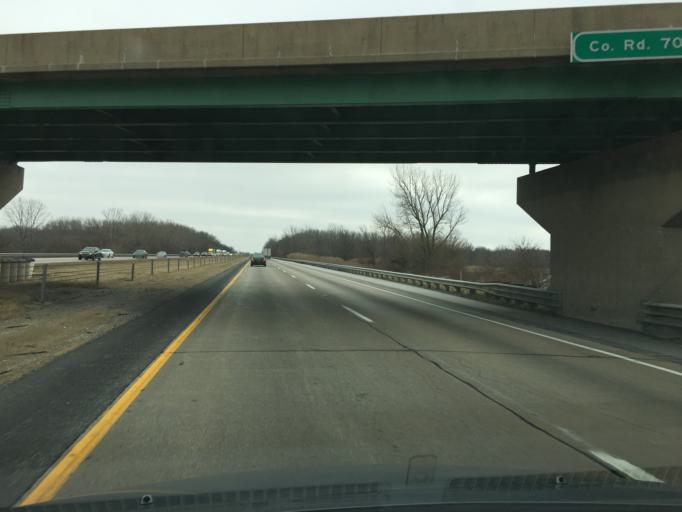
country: US
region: Indiana
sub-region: Jasper County
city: Rensselaer
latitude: 40.9122
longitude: -87.2132
